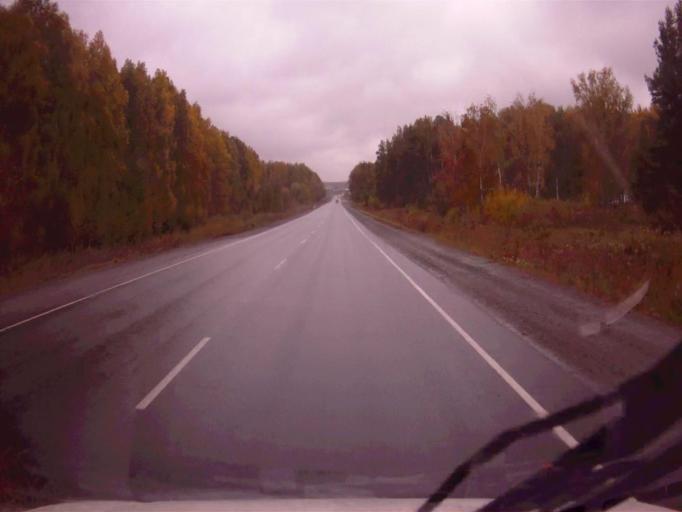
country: RU
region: Chelyabinsk
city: Roshchino
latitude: 55.3634
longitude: 61.2083
